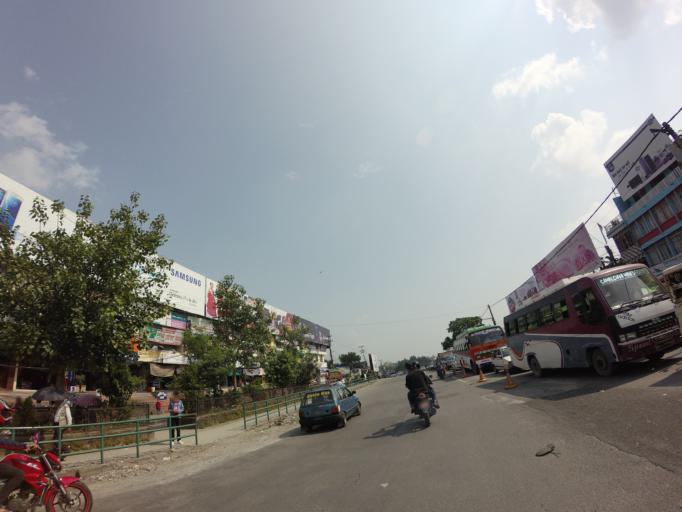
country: NP
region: Western Region
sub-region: Gandaki Zone
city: Pokhara
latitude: 28.2096
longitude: 83.9858
